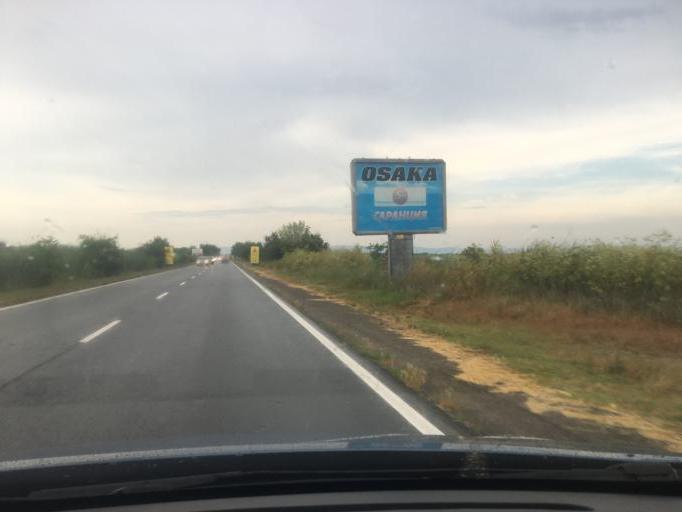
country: BG
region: Burgas
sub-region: Obshtina Pomorie
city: Pomorie
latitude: 42.5891
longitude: 27.6114
